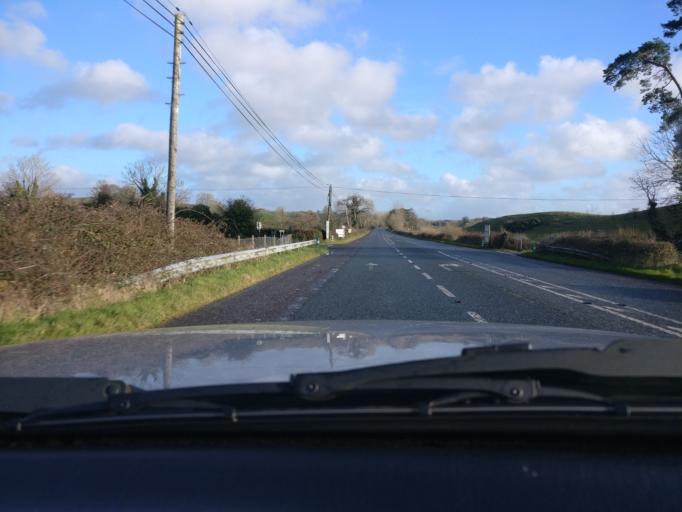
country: IE
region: Leinster
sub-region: Uibh Fhaili
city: Clara
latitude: 53.3984
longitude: -7.6069
